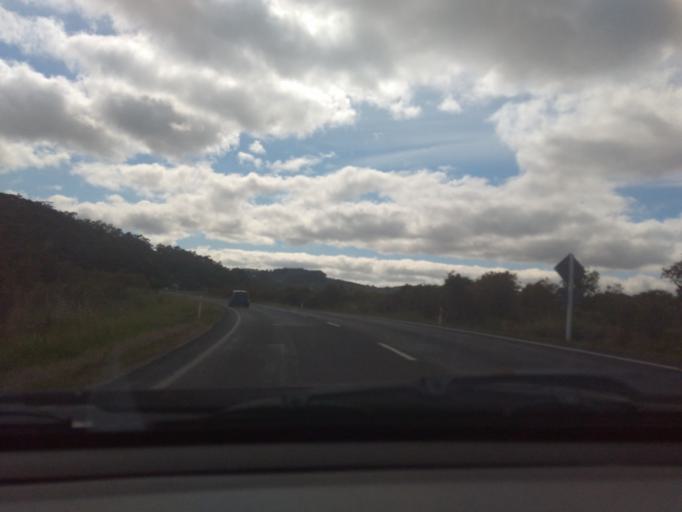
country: NZ
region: Northland
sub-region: Far North District
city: Taipa
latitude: -35.0117
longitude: 173.5442
